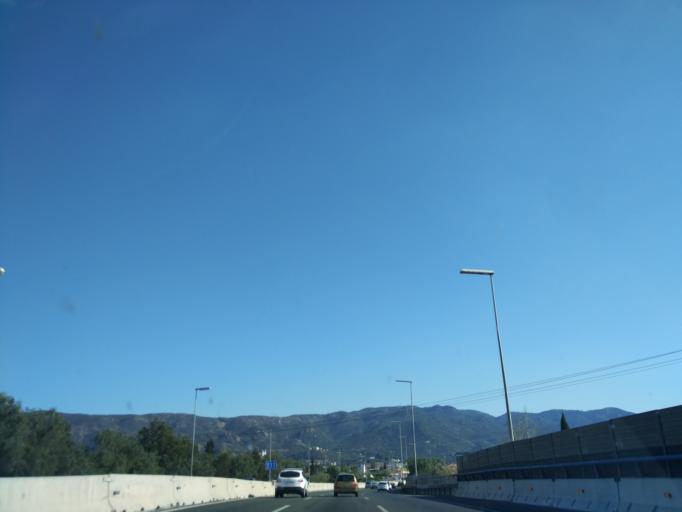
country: ES
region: Murcia
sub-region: Murcia
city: Murcia
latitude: 37.9644
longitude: -1.1360
